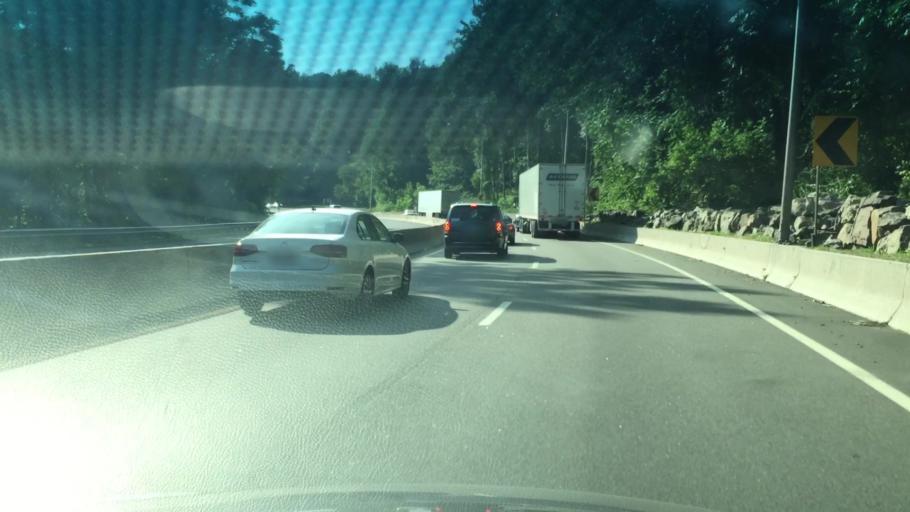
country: US
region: Pennsylvania
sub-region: Monroe County
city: East Stroudsburg
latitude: 40.9707
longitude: -75.1200
